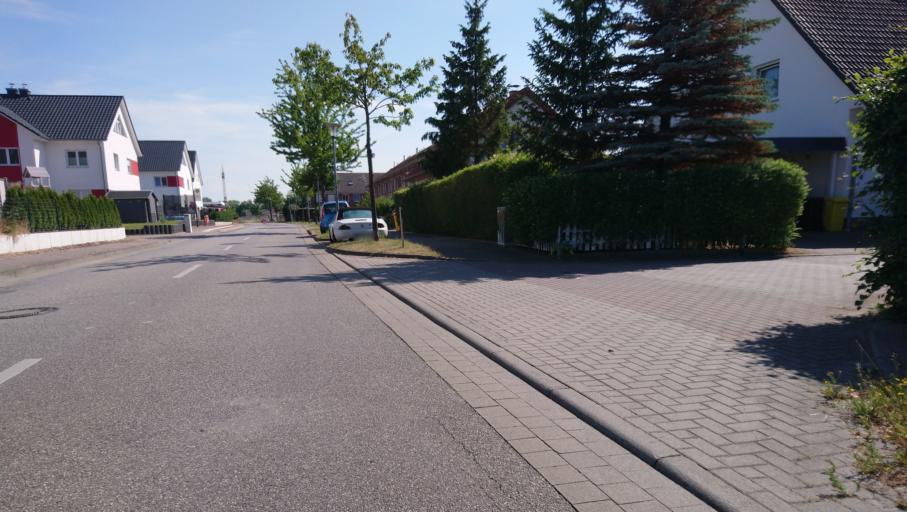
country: DE
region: Mecklenburg-Vorpommern
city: Roggentin
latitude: 54.0887
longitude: 12.1885
